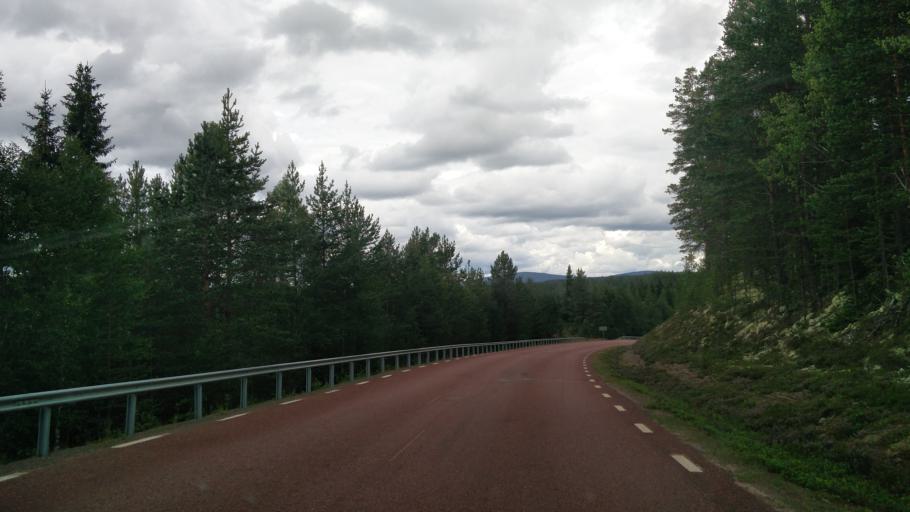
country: NO
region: Hedmark
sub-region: Trysil
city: Innbygda
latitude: 61.1484
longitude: 12.8013
